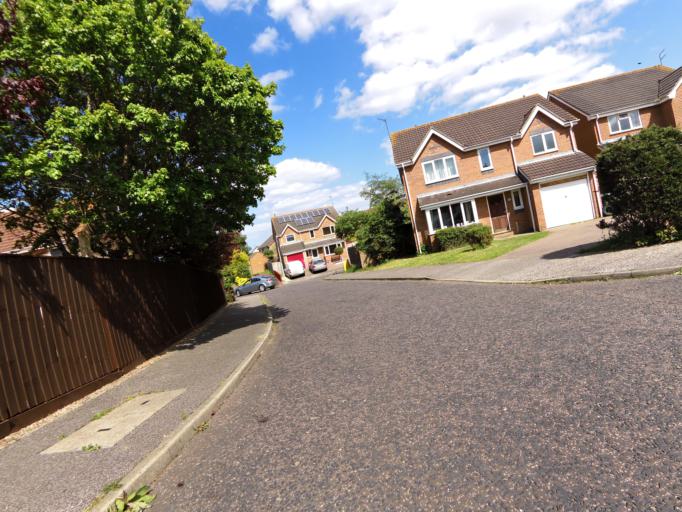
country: GB
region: England
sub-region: Suffolk
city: Kessingland
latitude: 52.4510
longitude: 1.7086
